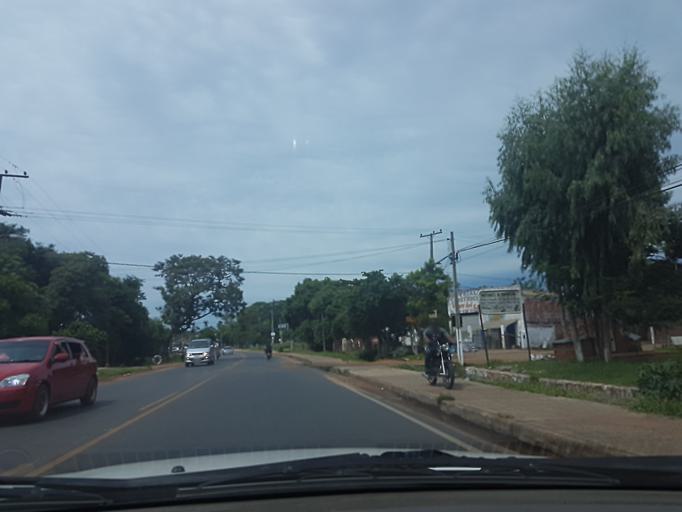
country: PY
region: Central
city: San Lorenzo
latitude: -25.2589
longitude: -57.4765
